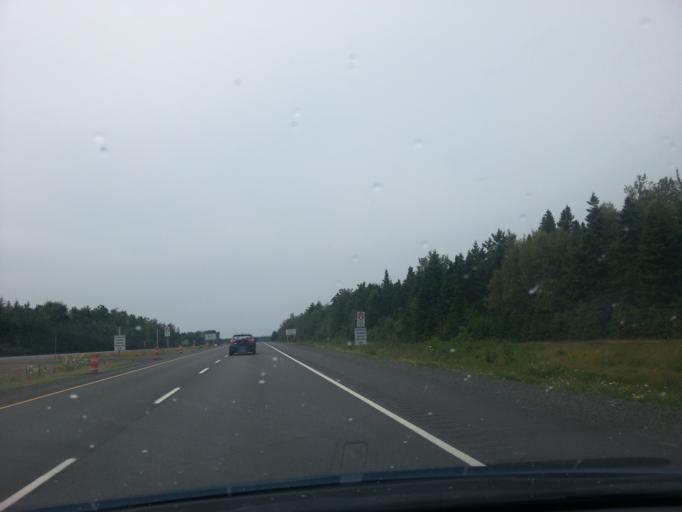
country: CA
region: Nova Scotia
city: Truro
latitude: 45.3965
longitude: -63.4764
